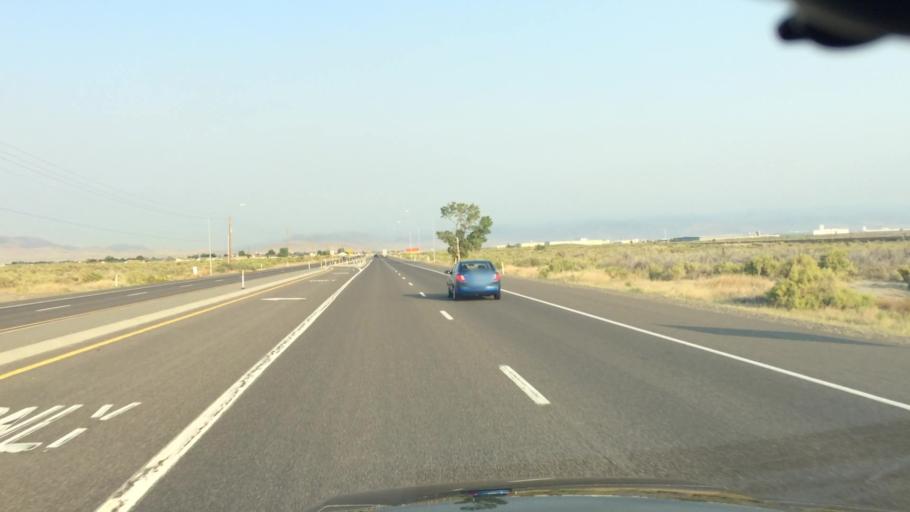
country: US
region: Nevada
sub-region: Lyon County
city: Fernley
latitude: 39.5959
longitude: -119.1784
